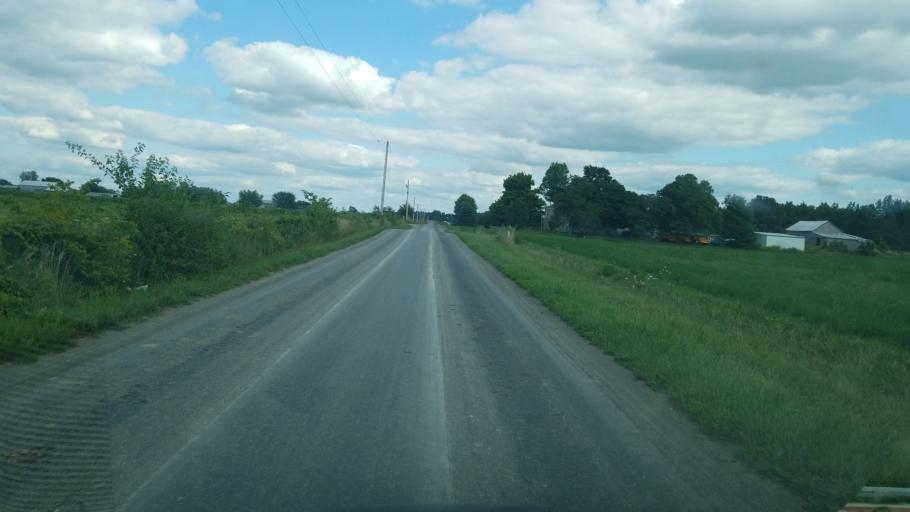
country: US
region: Ohio
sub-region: Logan County
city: De Graff
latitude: 40.3768
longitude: -83.8960
